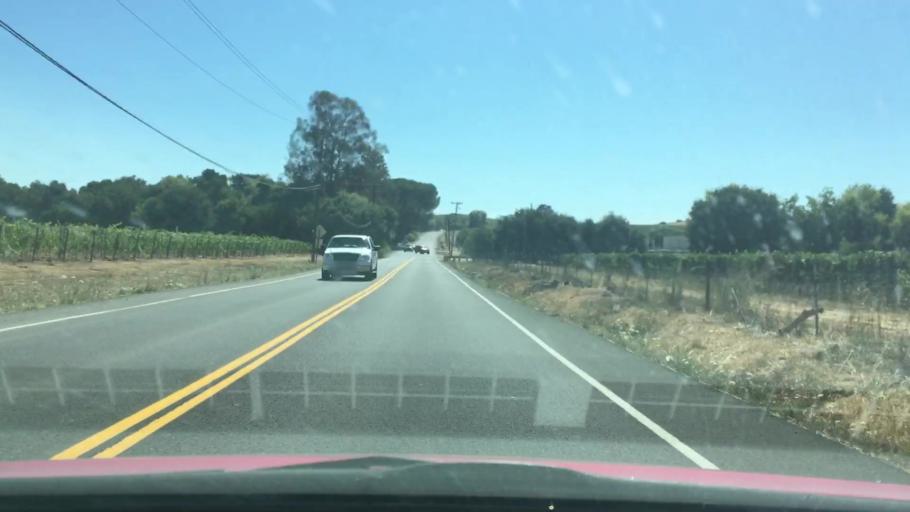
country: US
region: California
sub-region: Napa County
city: Napa
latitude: 38.2715
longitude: -122.3305
